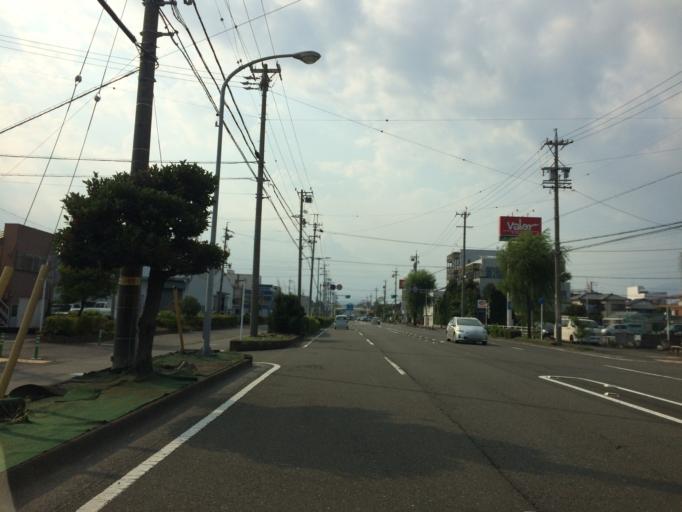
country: JP
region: Shizuoka
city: Shizuoka-shi
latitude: 34.9597
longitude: 138.4154
